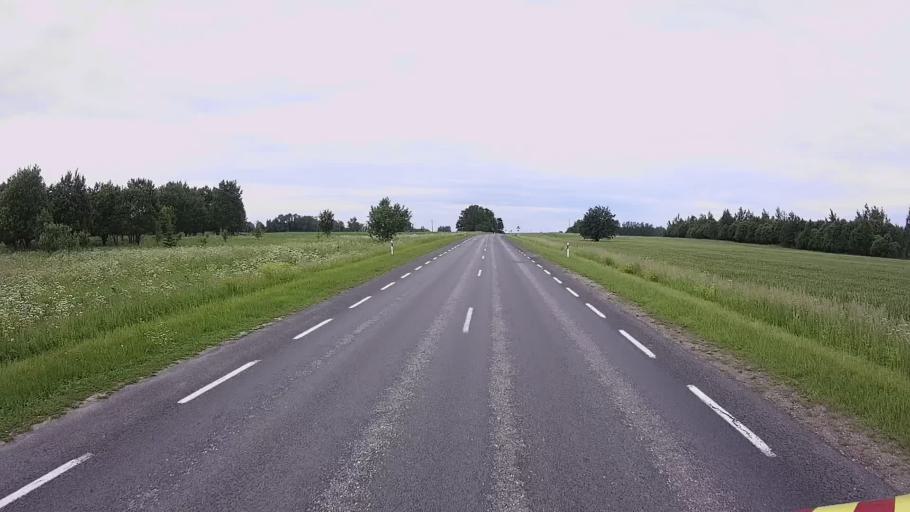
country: EE
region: Viljandimaa
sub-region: Karksi vald
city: Karksi-Nuia
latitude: 58.1815
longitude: 25.5923
